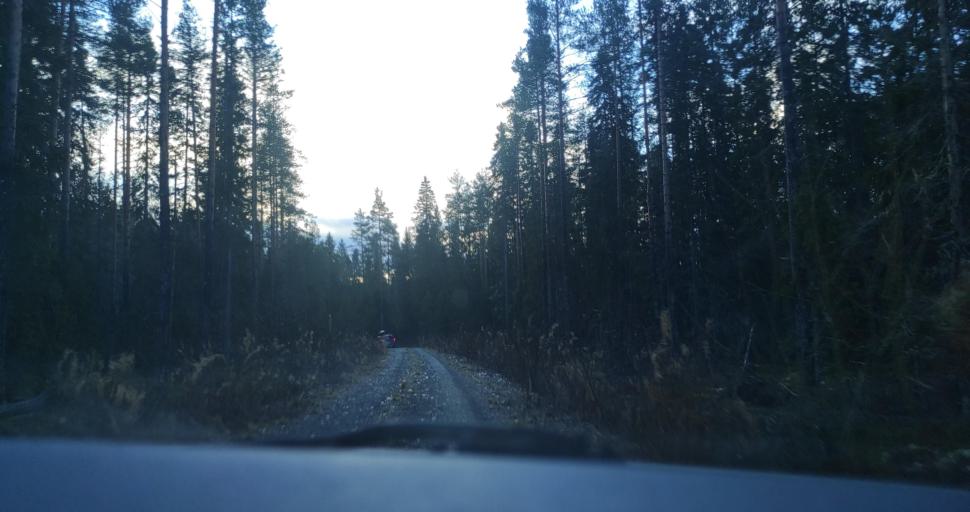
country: RU
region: Republic of Karelia
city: Pitkyaranta
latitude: 61.7348
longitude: 31.3659
